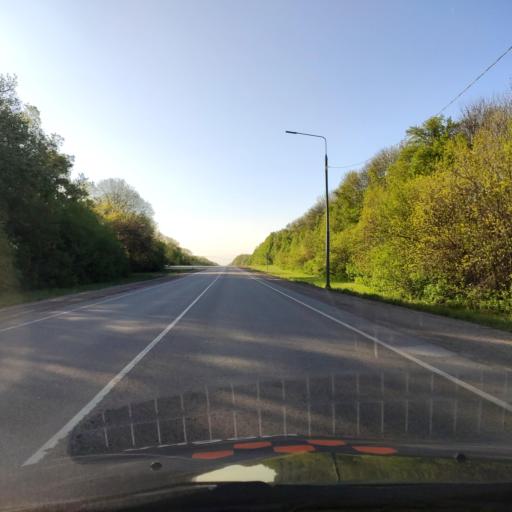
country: RU
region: Lipetsk
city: Yelets
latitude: 52.5794
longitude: 38.6384
